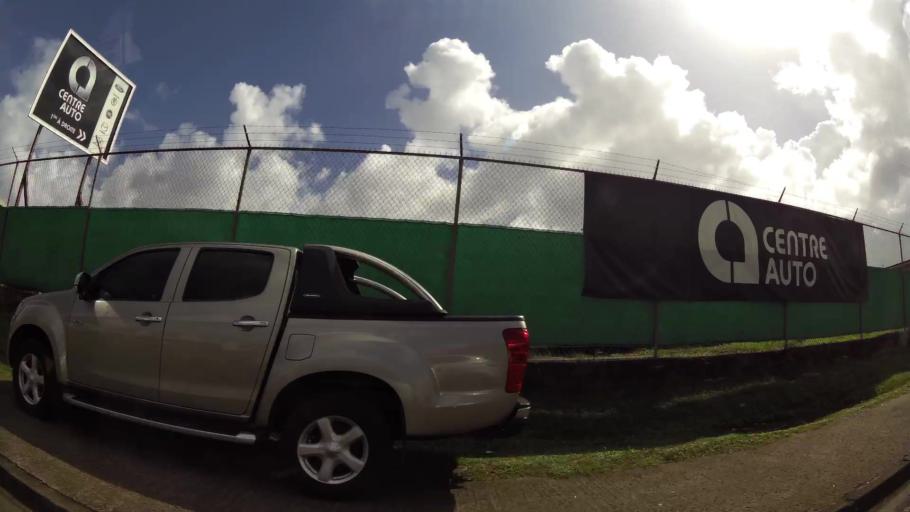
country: MQ
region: Martinique
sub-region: Martinique
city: Le Lamentin
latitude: 14.6150
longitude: -60.9925
